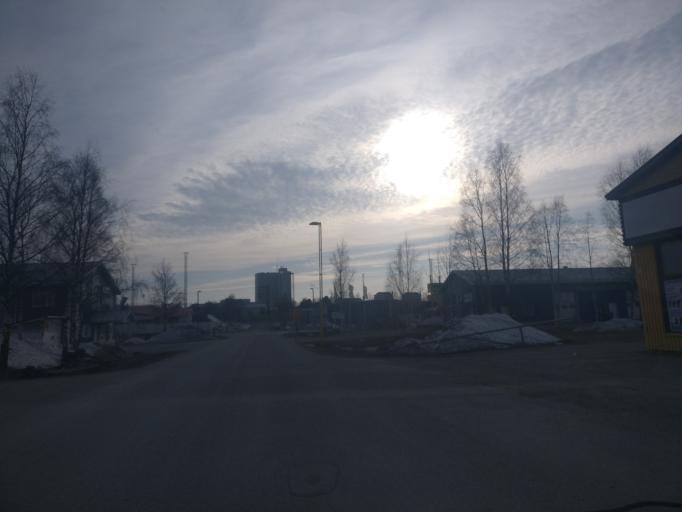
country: FI
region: Lapland
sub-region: Kemi-Tornio
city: Kemi
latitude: 65.7376
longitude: 24.5823
